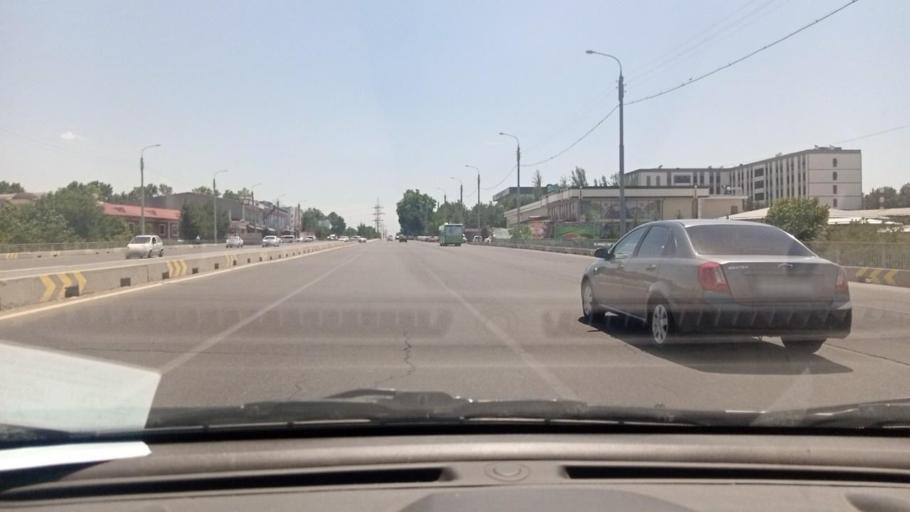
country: UZ
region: Toshkent Shahri
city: Tashkent
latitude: 41.3035
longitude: 69.1937
